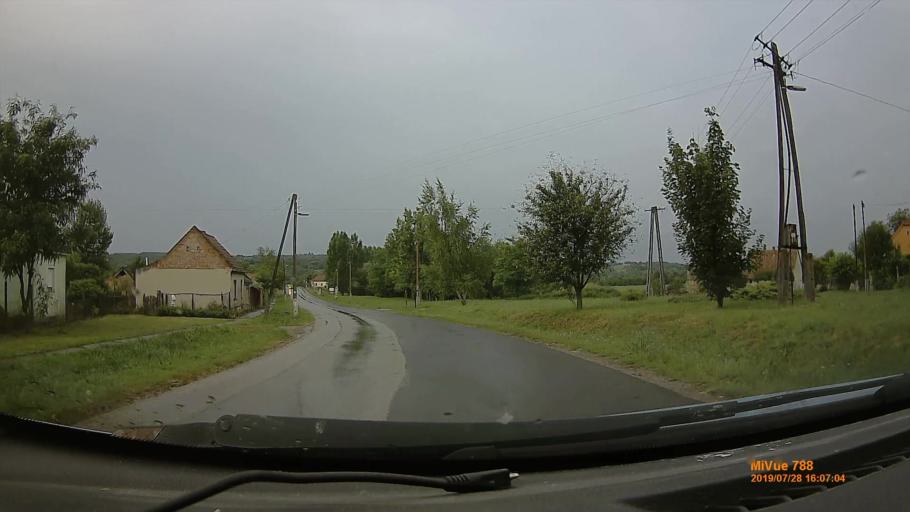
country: HU
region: Baranya
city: Buekkoesd
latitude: 46.0836
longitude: 17.9896
